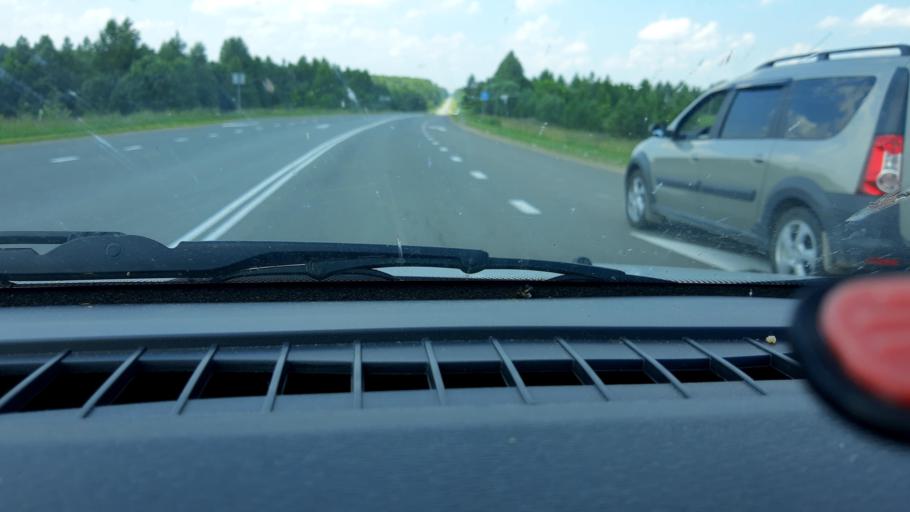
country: RU
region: Nizjnij Novgorod
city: Sharanga
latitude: 57.2156
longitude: 46.5058
